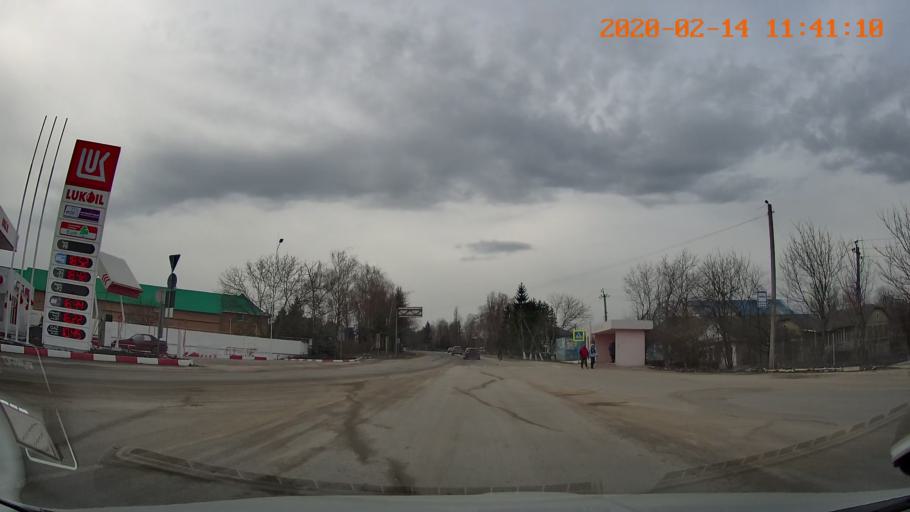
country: MD
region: Briceni
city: Briceni
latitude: 48.3506
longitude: 27.0837
